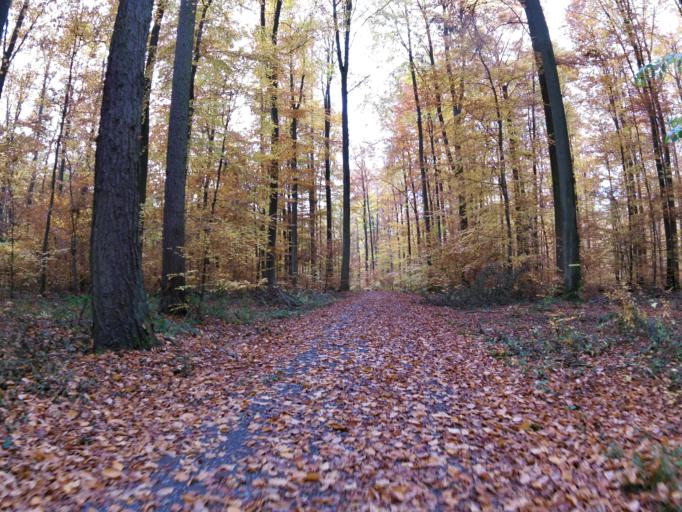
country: DE
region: Bavaria
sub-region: Regierungsbezirk Unterfranken
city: Kist
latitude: 49.7311
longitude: 9.8304
